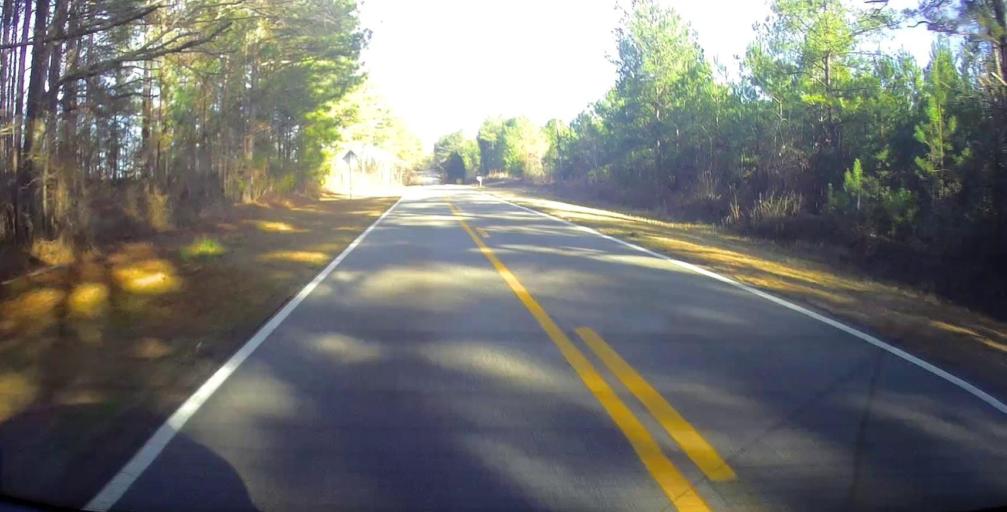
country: US
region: Georgia
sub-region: Crawford County
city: Roberta
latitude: 32.7712
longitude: -84.1103
